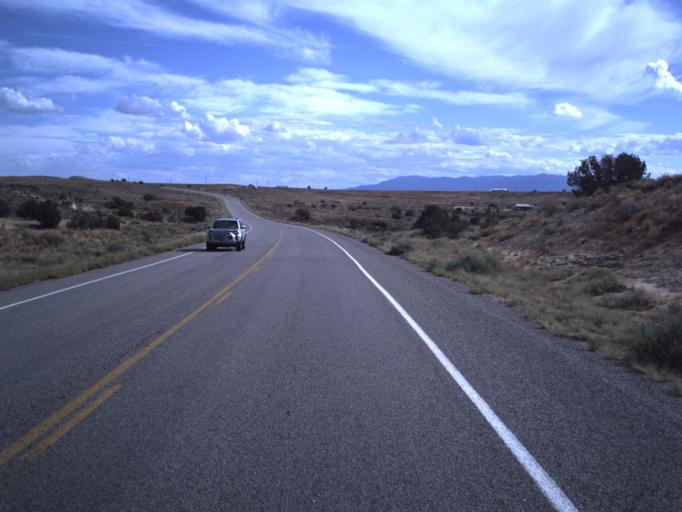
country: US
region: Colorado
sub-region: Montezuma County
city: Towaoc
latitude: 37.1865
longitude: -109.1270
